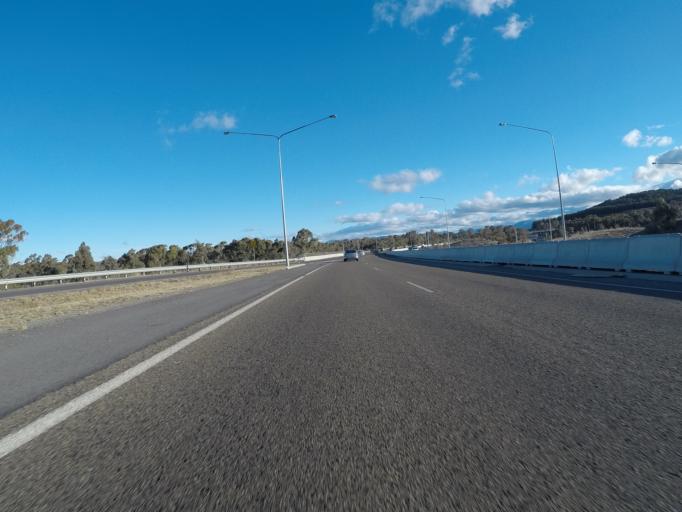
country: AU
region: Australian Capital Territory
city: Acton
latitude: -35.2833
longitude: 149.0857
